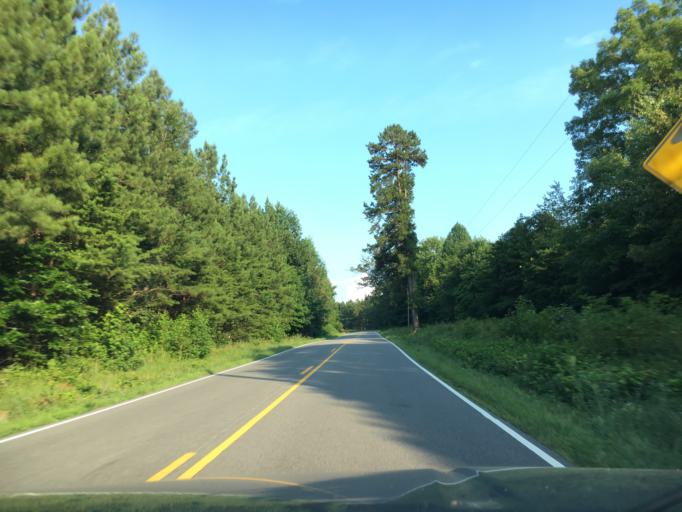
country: US
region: Virginia
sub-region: Pittsylvania County
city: Chatham
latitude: 36.8161
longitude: -79.2695
